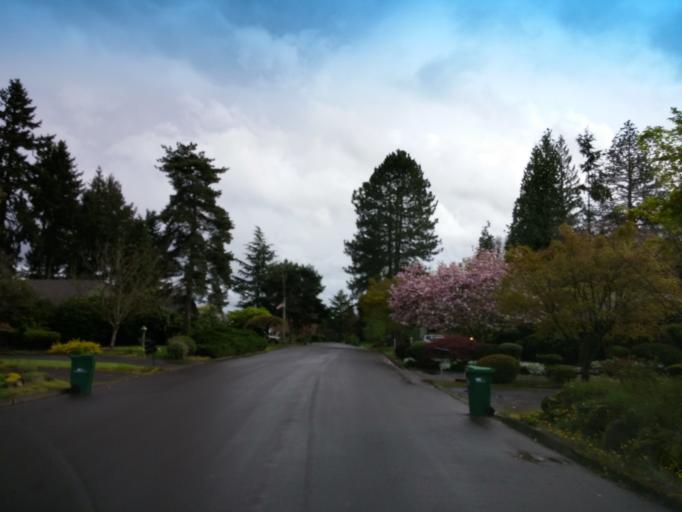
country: US
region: Oregon
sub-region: Washington County
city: Cedar Mill
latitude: 45.5188
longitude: -122.8249
